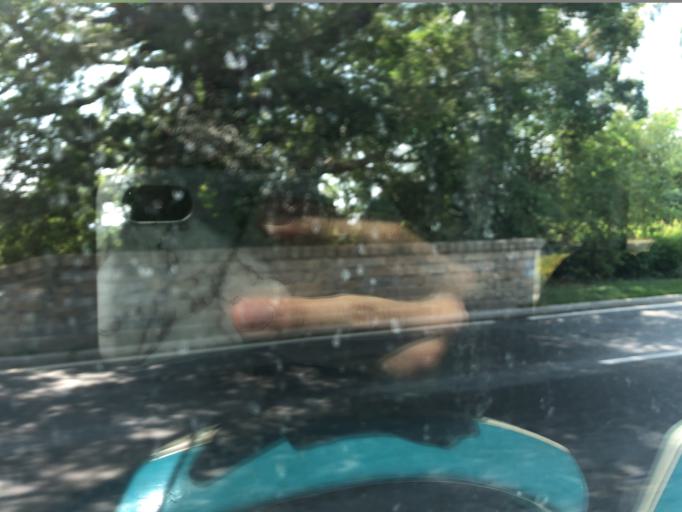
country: CN
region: Fujian
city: Xiamen
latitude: 24.4264
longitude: 118.1271
